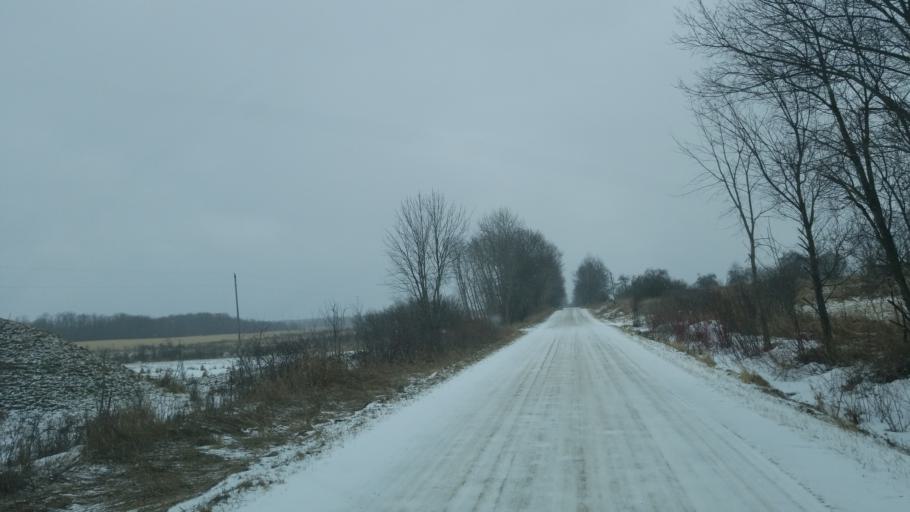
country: US
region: Michigan
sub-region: Osceola County
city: Evart
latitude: 44.0159
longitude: -85.2198
